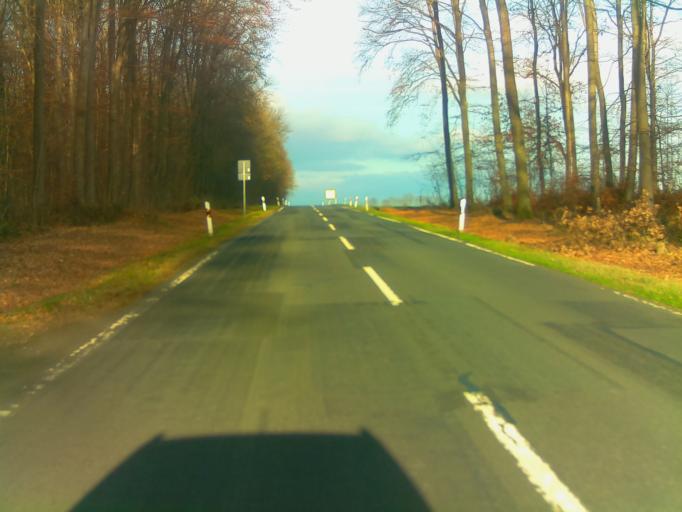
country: DE
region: Bavaria
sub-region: Regierungsbezirk Unterfranken
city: Eichenbuhl
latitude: 49.6981
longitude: 9.3597
